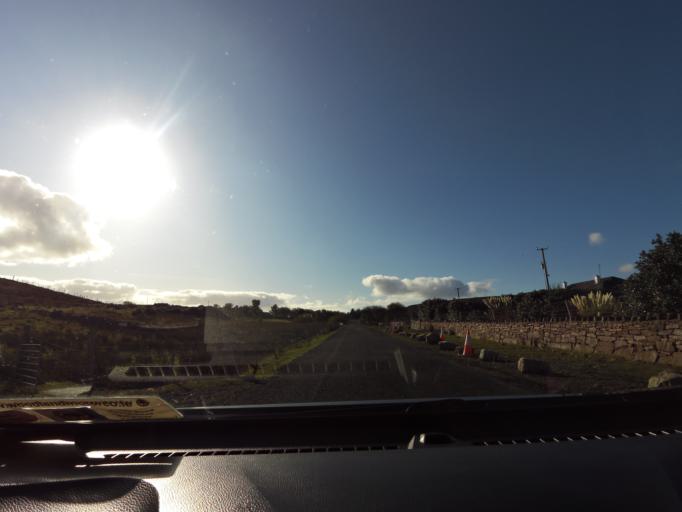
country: IE
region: Connaught
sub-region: Maigh Eo
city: Westport
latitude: 53.8869
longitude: -9.8060
